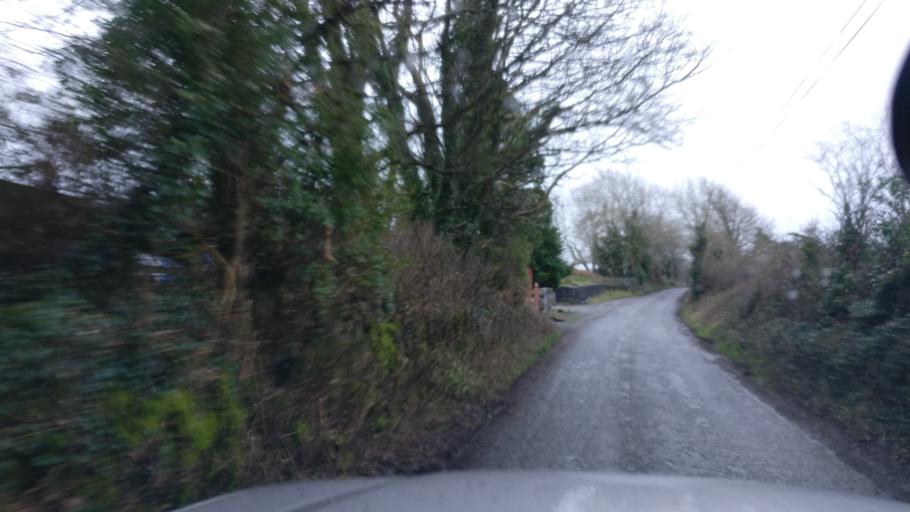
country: IE
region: Connaught
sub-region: County Galway
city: Loughrea
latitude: 53.1903
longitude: -8.6610
